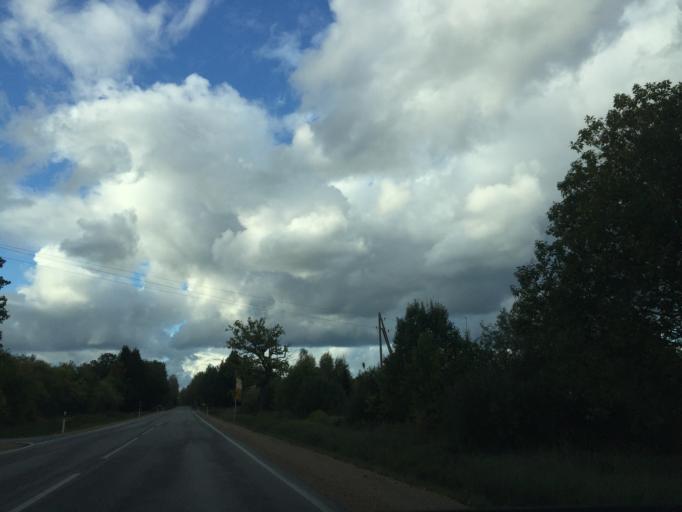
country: LV
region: Ligatne
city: Ligatne
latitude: 57.1752
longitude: 25.0410
